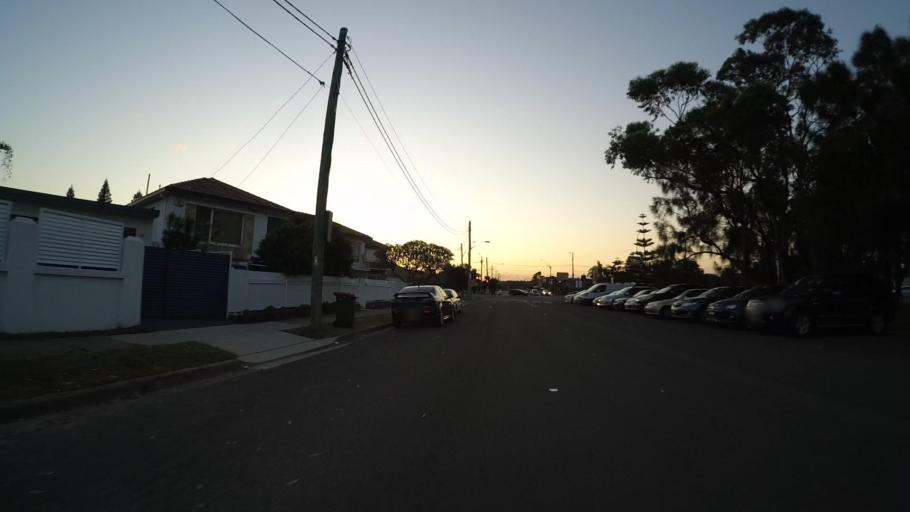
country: AU
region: New South Wales
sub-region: Rockdale
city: Brighton-Le-Sands
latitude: -33.9519
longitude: 151.1622
